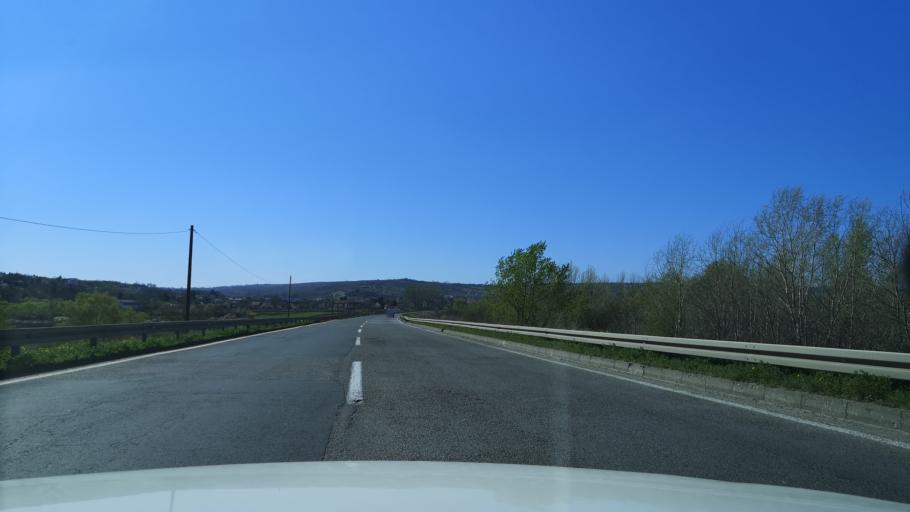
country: RS
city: Ostruznica
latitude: 44.7059
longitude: 20.3183
